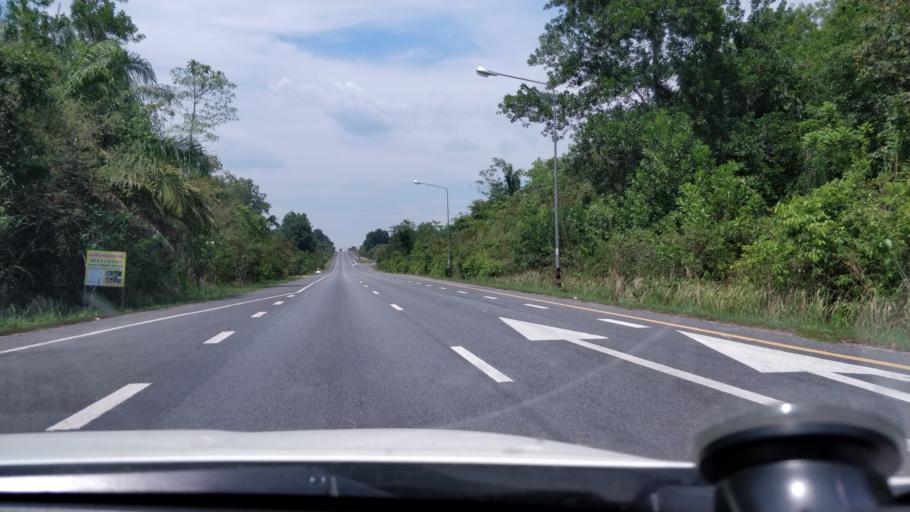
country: TH
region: Surat Thani
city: Phrasaeng
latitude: 8.6631
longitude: 99.1130
